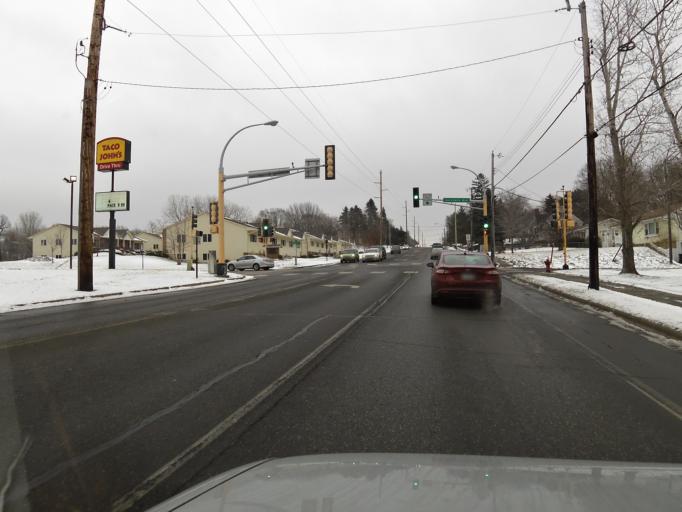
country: US
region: Minnesota
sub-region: Ramsey County
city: Maplewood
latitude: 44.9632
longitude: -92.9820
